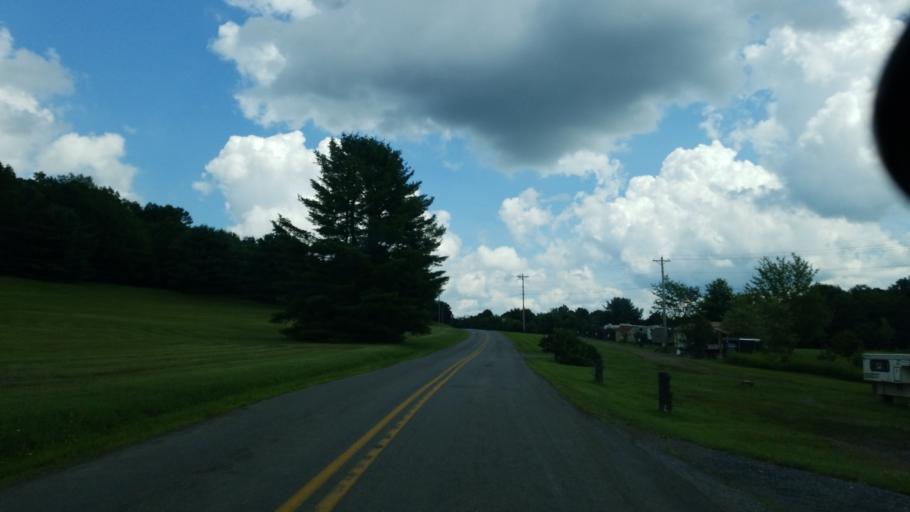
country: US
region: Pennsylvania
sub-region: Jefferson County
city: Brookville
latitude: 41.2320
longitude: -79.0672
